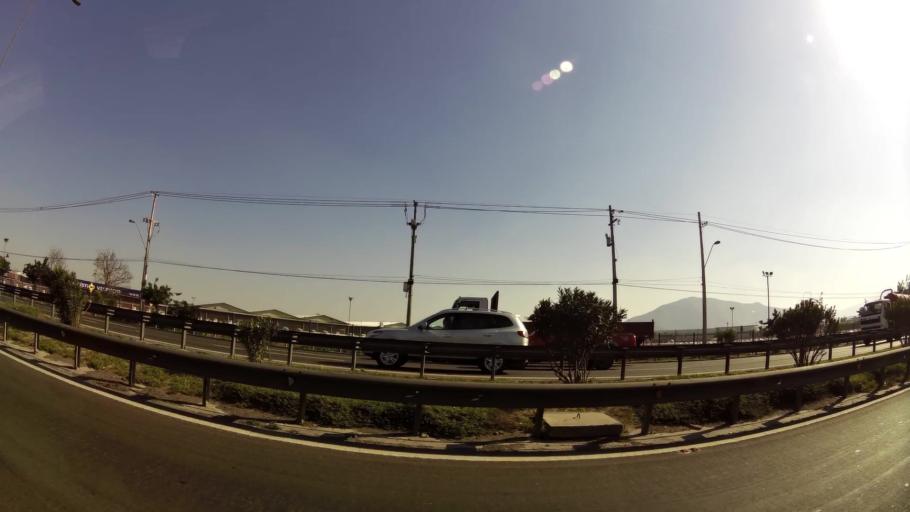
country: CL
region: Santiago Metropolitan
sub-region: Provincia de Santiago
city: Lo Prado
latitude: -33.4527
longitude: -70.7712
